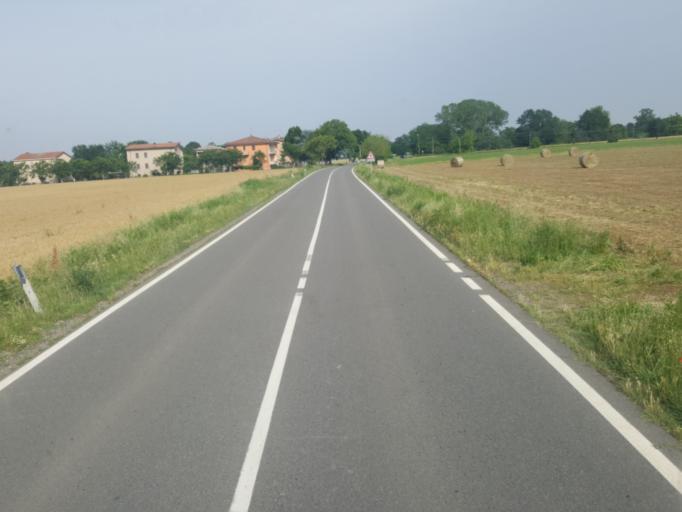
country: IT
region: Emilia-Romagna
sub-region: Provincia di Piacenza
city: Niviano
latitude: 44.9402
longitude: 9.6376
